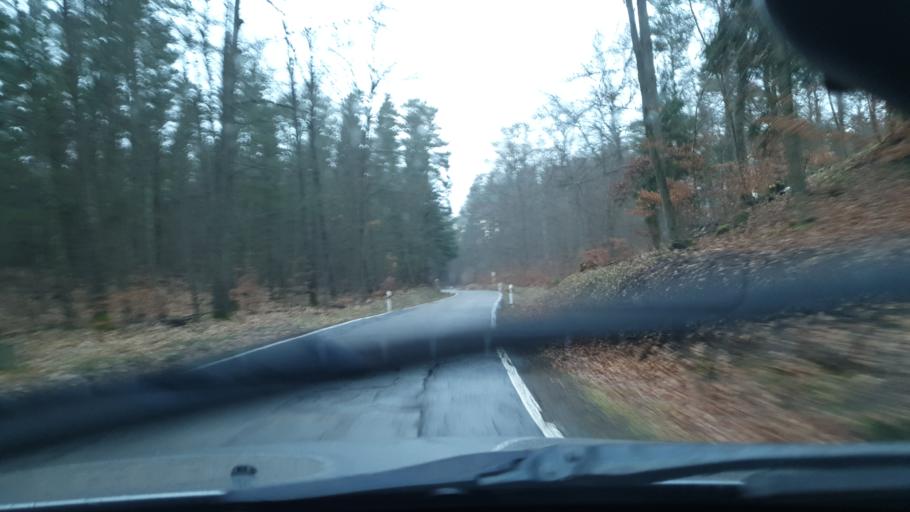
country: DE
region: Rheinland-Pfalz
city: Kaiserslautern
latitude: 49.4224
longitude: 7.7689
